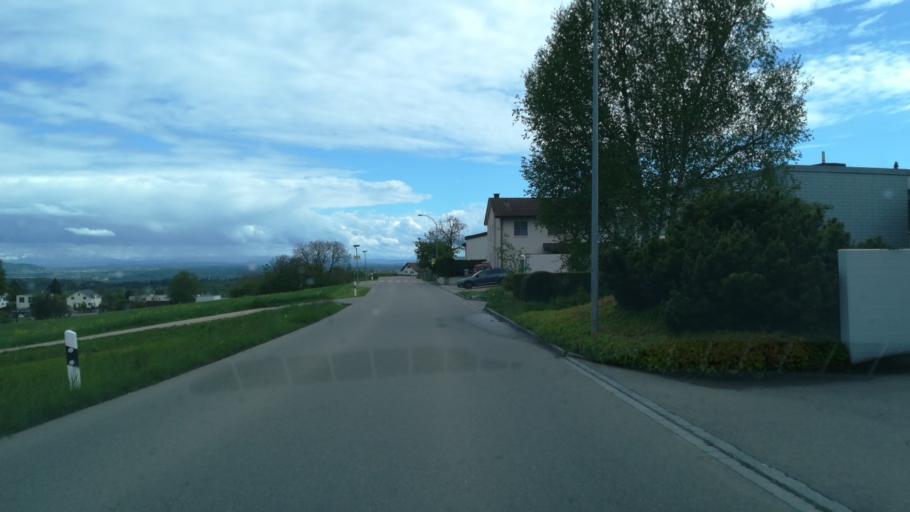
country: CH
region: Schaffhausen
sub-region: Bezirk Reiat
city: Stetten
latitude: 47.7438
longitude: 8.6628
